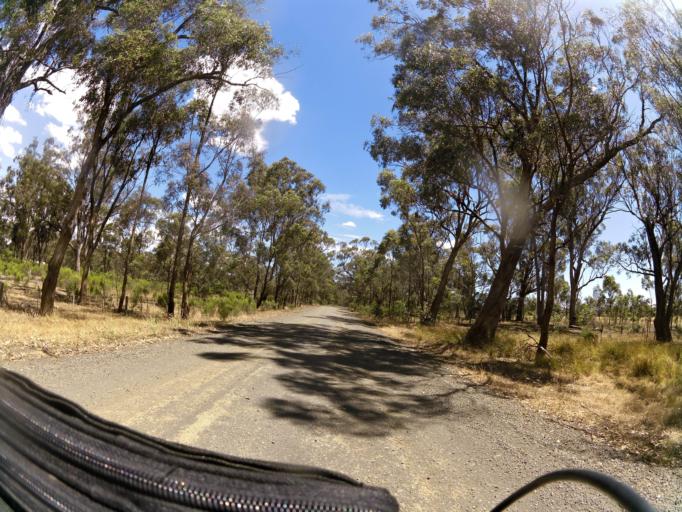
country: AU
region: Victoria
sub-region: Campaspe
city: Kyabram
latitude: -36.7996
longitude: 145.0784
